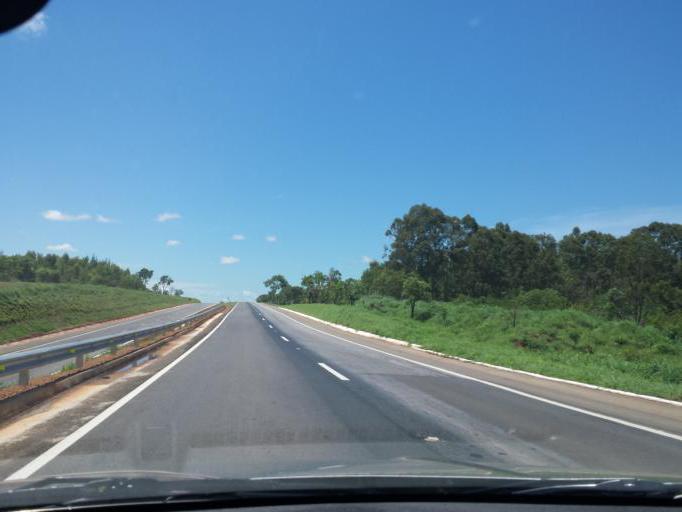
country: BR
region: Goias
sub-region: Luziania
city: Luziania
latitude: -16.4702
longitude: -47.8089
